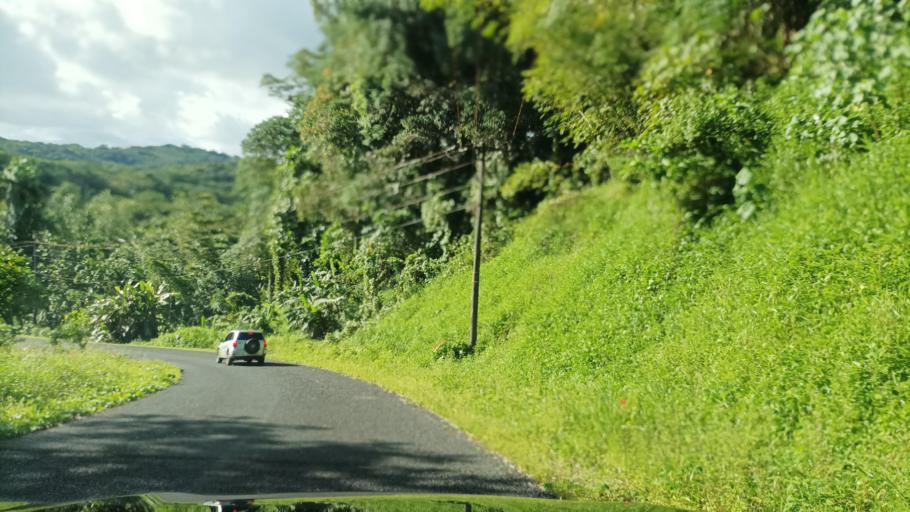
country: FM
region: Pohnpei
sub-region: Sokehs Municipality
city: Palikir - National Government Center
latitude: 6.8233
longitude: 158.1736
